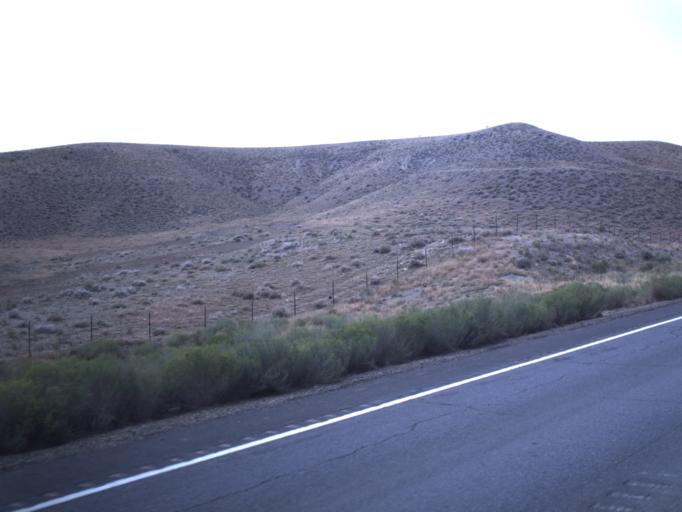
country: US
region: Utah
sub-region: Duchesne County
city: Duchesne
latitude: 40.1549
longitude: -110.2473
